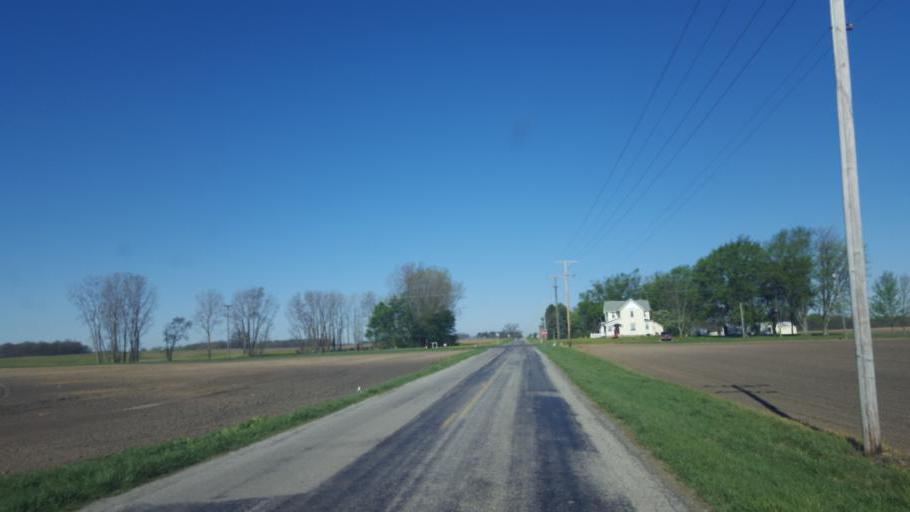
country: US
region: Ohio
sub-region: Crawford County
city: Bucyrus
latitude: 40.6741
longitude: -83.0112
